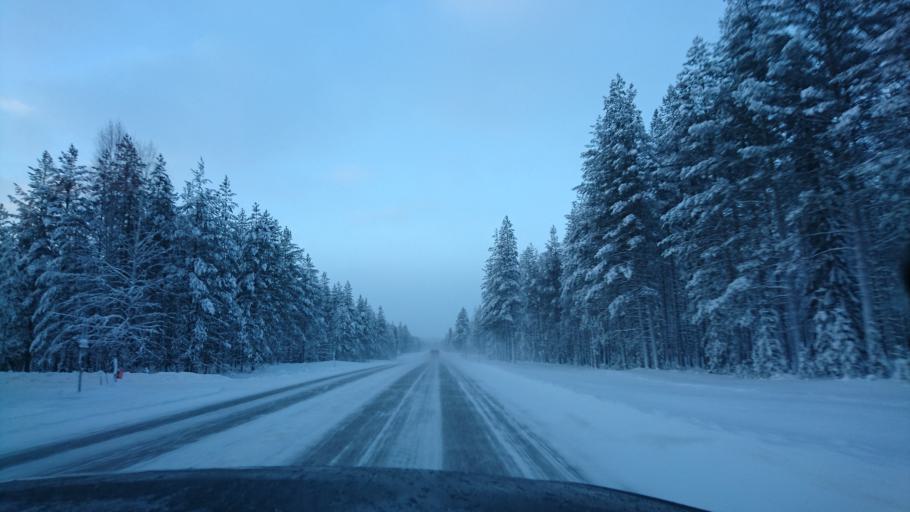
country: FI
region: Northern Ostrobothnia
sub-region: Koillismaa
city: Taivalkoski
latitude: 65.4856
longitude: 27.8356
